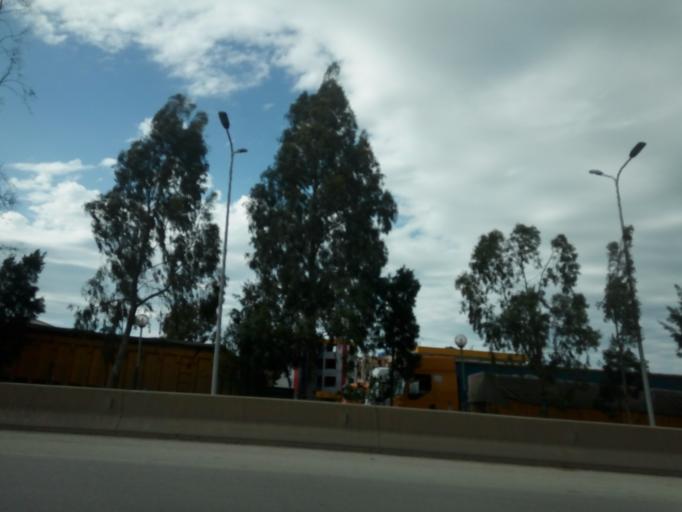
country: DZ
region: Blida
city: Chiffa
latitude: 36.4527
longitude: 2.7341
